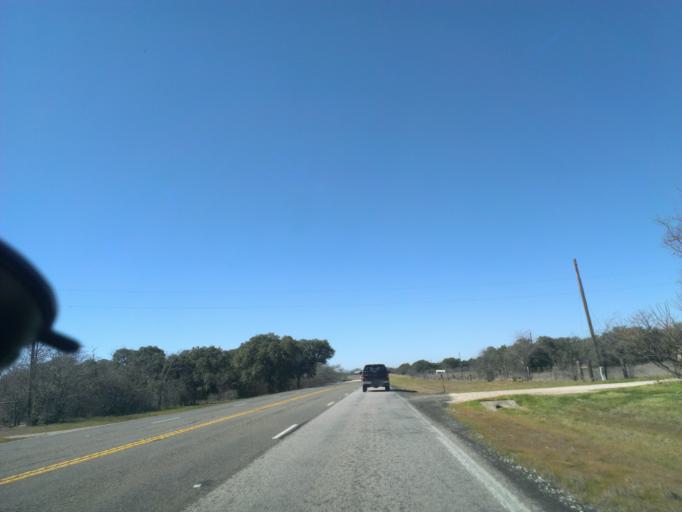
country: US
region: Texas
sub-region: Williamson County
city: Florence
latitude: 30.8900
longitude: -97.9401
